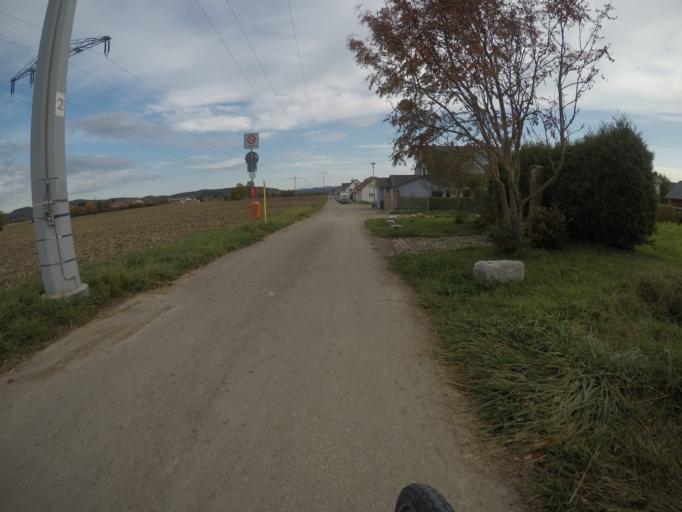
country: DE
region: Baden-Wuerttemberg
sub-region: Tuebingen Region
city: Rottenburg
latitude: 48.5398
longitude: 8.9450
